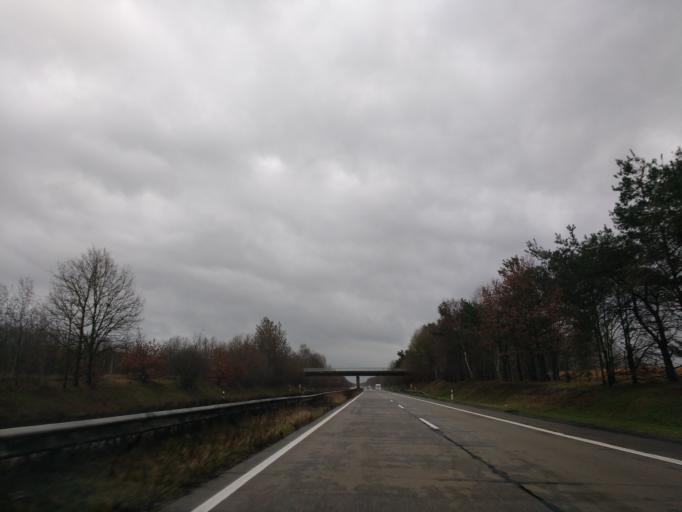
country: DE
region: Lower Saxony
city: Midlum
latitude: 53.6603
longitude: 8.6593
